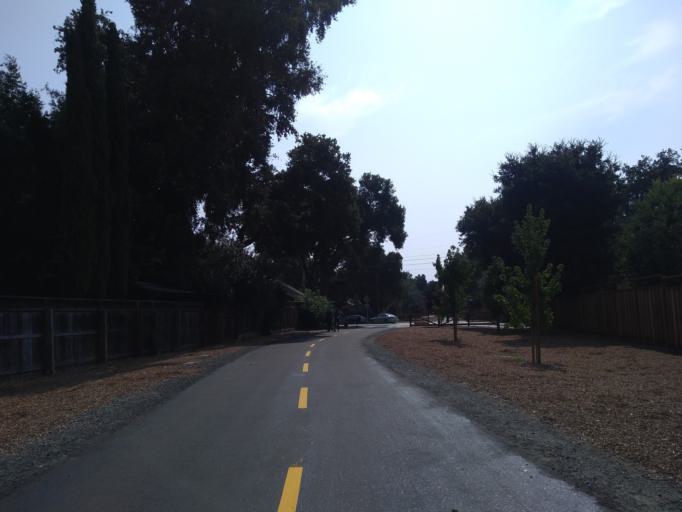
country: US
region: California
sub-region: Santa Clara County
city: Buena Vista
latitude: 37.3123
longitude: -121.9005
